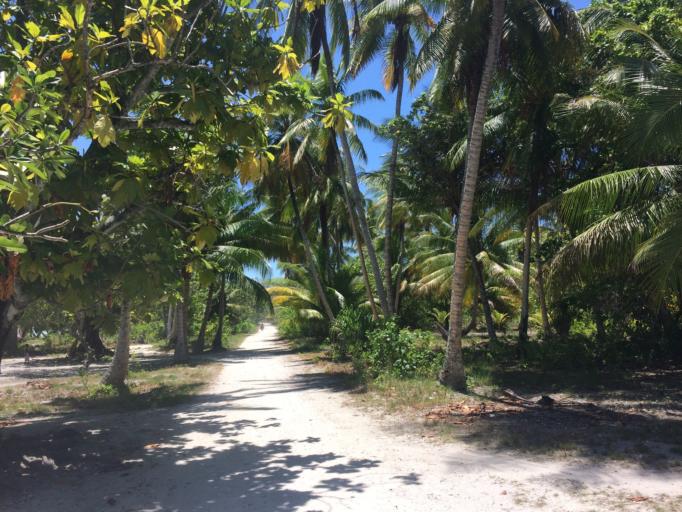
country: KI
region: Gilbert Islands
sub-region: Marakei
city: Rawannawi Village
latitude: 1.7536
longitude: 173.0413
